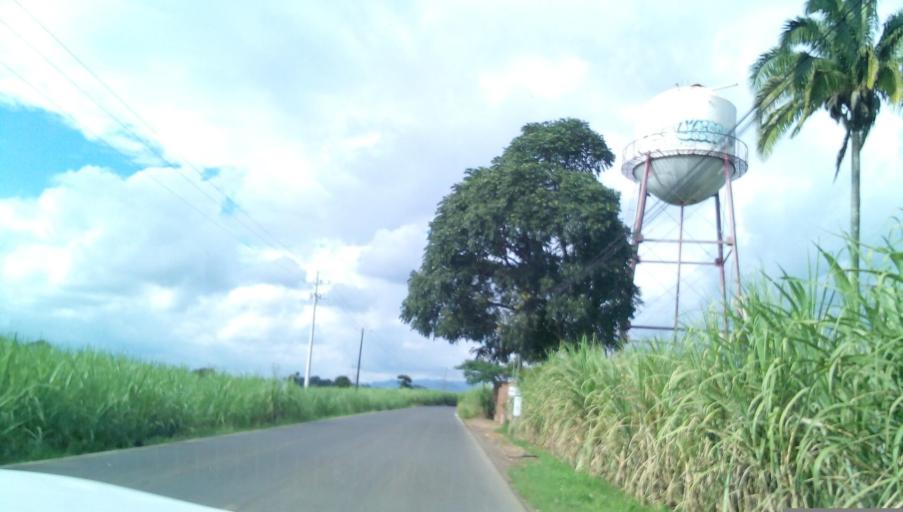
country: MX
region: Veracruz
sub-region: Amatlan de los Reyes
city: Centro de Readaptacion Social
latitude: 18.8252
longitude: -96.9244
